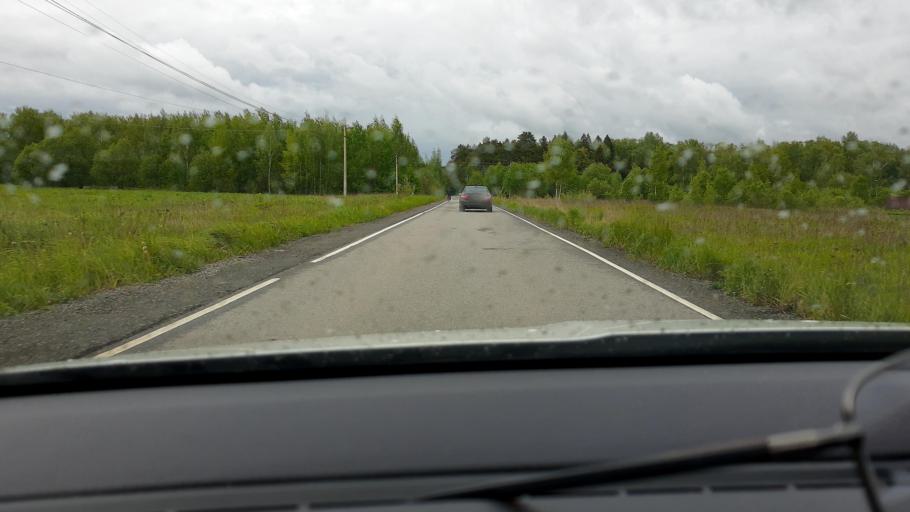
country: RU
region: Moskovskaya
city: Nikolina Gora
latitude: 55.7567
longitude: 36.9810
